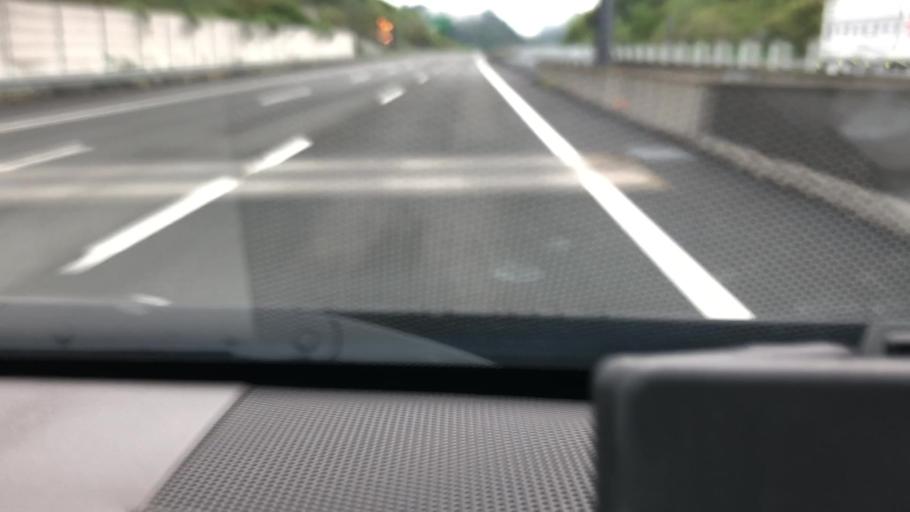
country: JP
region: Shizuoka
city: Fujieda
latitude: 34.9081
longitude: 138.2518
